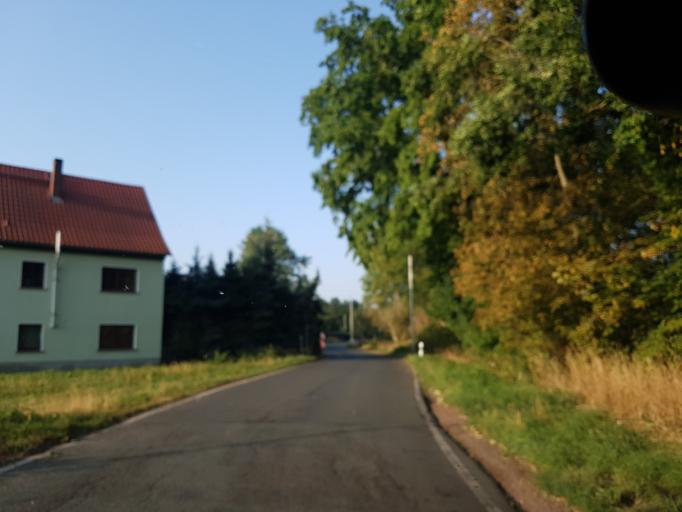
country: DE
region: Saxony
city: Strehla
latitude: 51.3125
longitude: 13.1951
